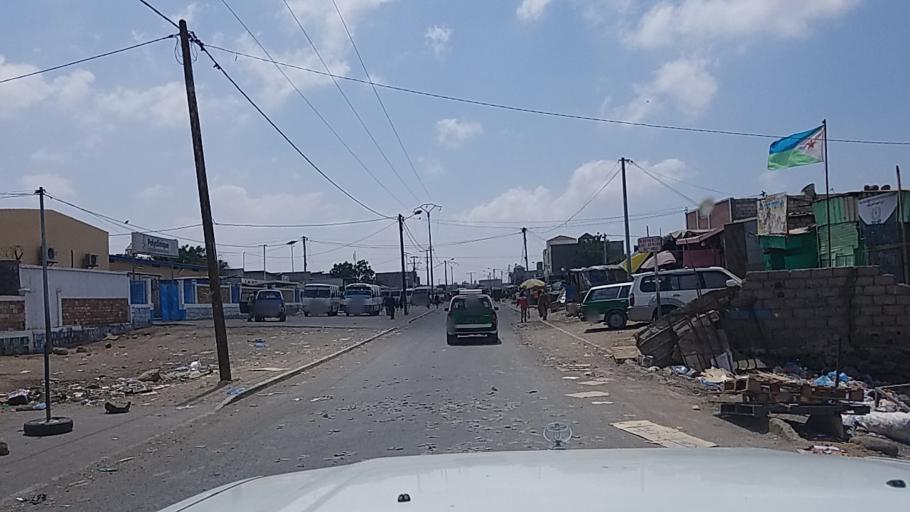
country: DJ
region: Djibouti
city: Djibouti
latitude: 11.5574
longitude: 43.0823
